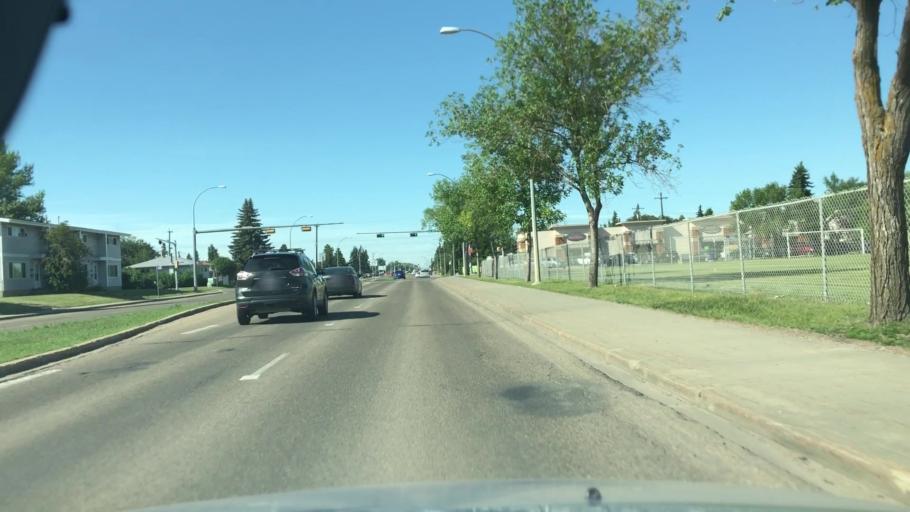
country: CA
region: Alberta
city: Edmonton
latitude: 53.5939
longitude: -113.5165
